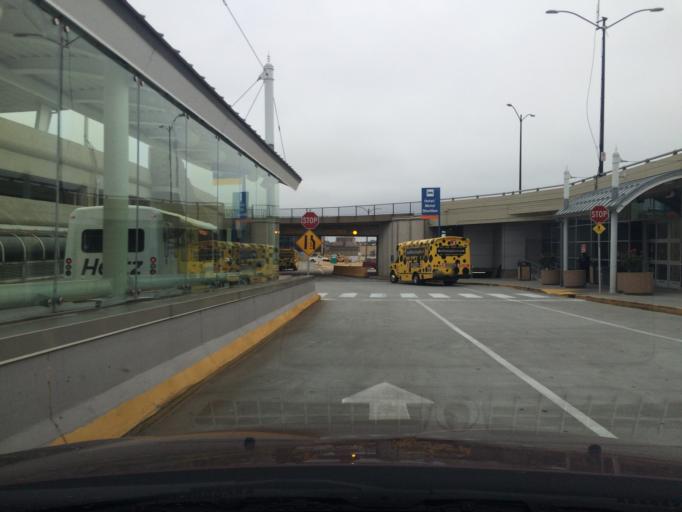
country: US
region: Missouri
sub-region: Saint Louis County
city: Woodson Terrace
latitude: 38.7426
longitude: -90.3672
